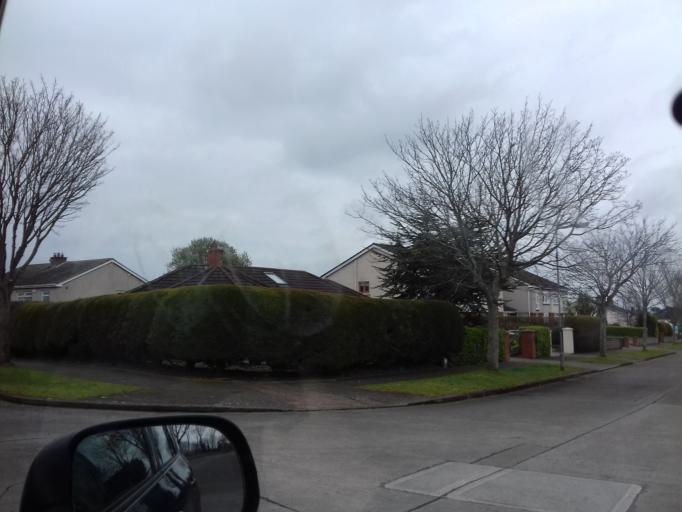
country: IE
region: Leinster
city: Portmarnock
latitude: 53.4376
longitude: -6.1319
